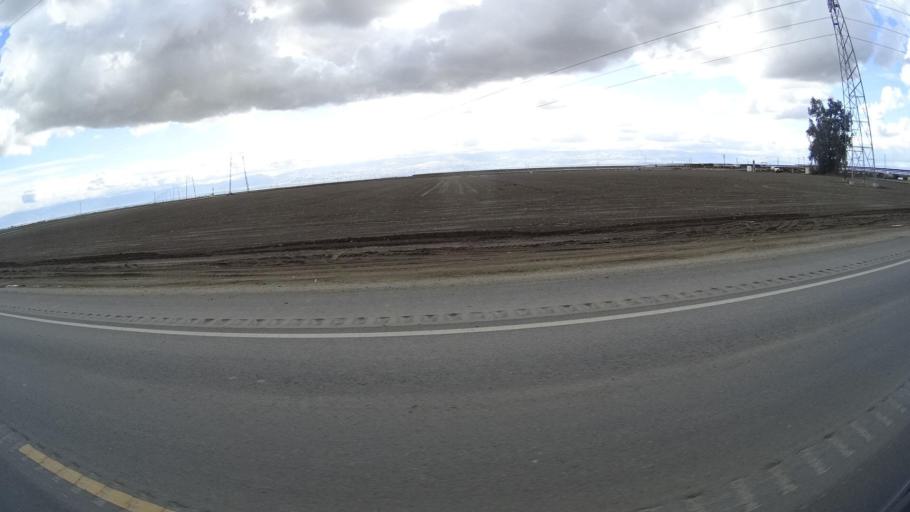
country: US
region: California
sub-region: Kern County
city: Greenfield
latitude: 35.2090
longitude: -119.0773
